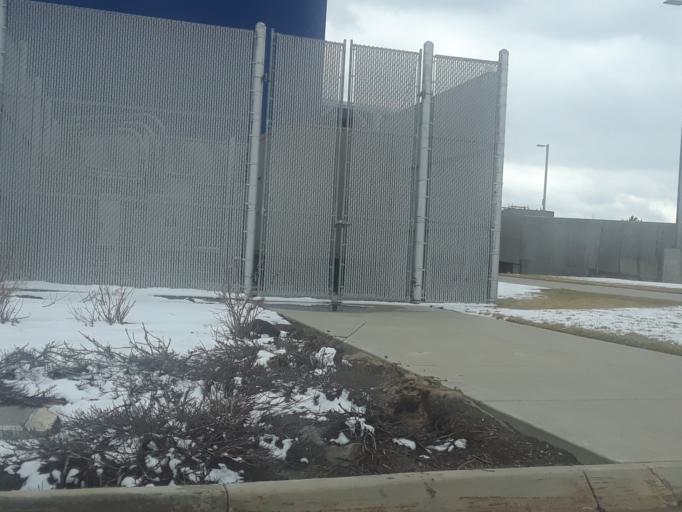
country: US
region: Colorado
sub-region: Arapahoe County
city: Centennial
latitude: 39.5732
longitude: -104.8758
